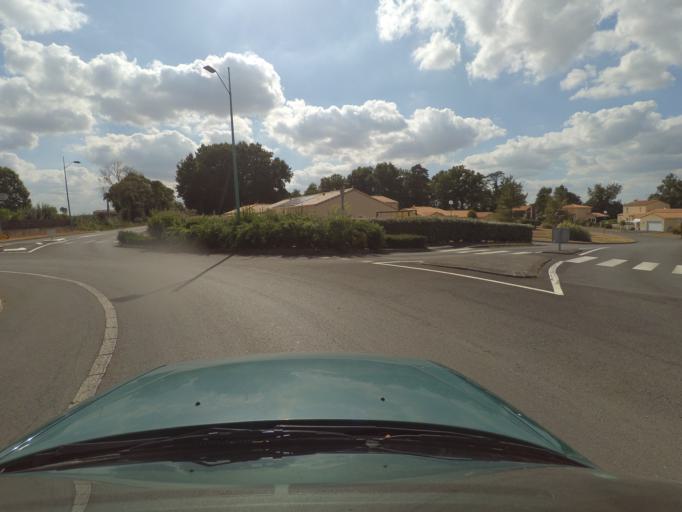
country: FR
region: Pays de la Loire
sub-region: Departement de la Loire-Atlantique
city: Aigrefeuille-sur-Maine
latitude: 47.0706
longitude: -1.4014
